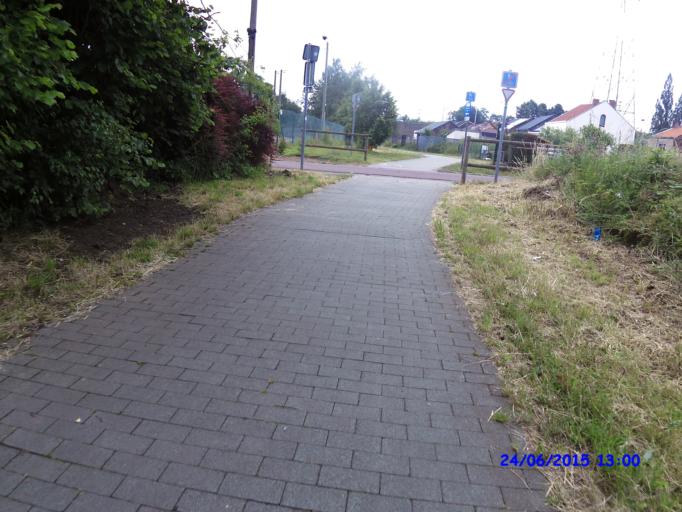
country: BE
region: Wallonia
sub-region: Province de Liege
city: Ans
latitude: 50.6557
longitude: 5.5223
